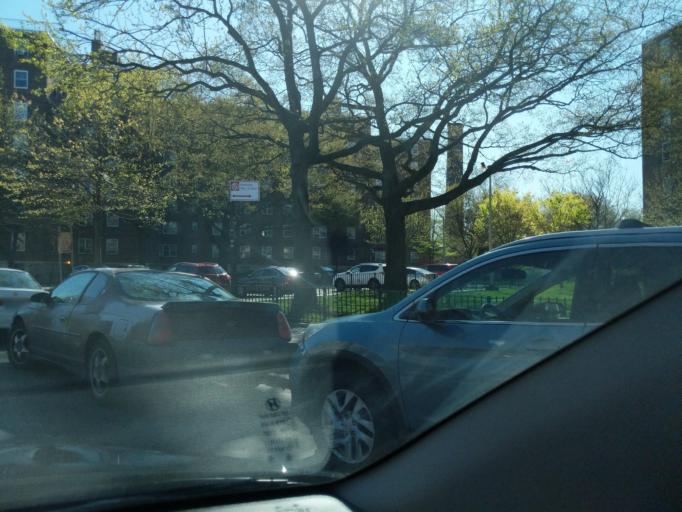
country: US
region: New York
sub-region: Kings County
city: East New York
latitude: 40.6510
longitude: -73.8972
